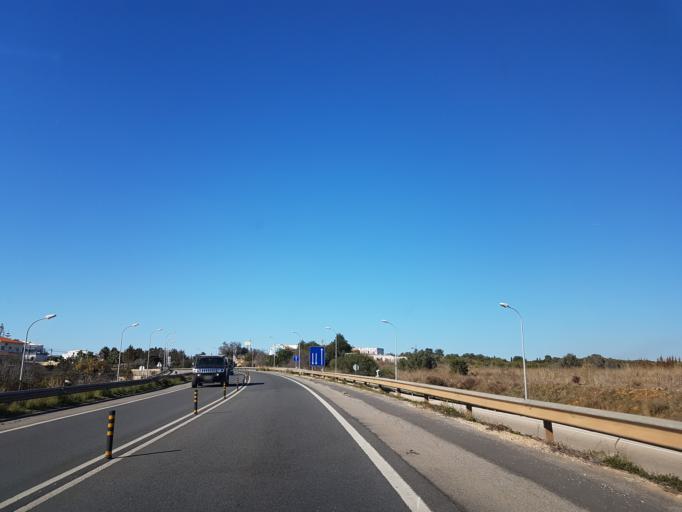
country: PT
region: Faro
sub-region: Portimao
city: Portimao
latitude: 37.1617
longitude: -8.5573
